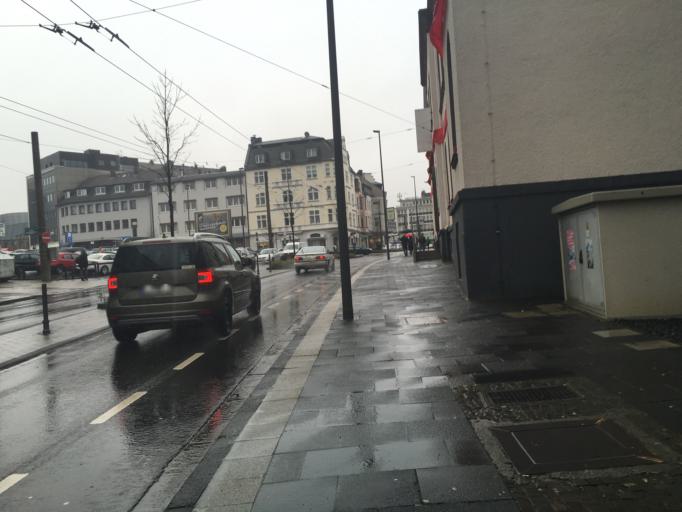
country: DE
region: North Rhine-Westphalia
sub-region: Regierungsbezirk Dusseldorf
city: Solingen
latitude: 51.1689
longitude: 7.0817
